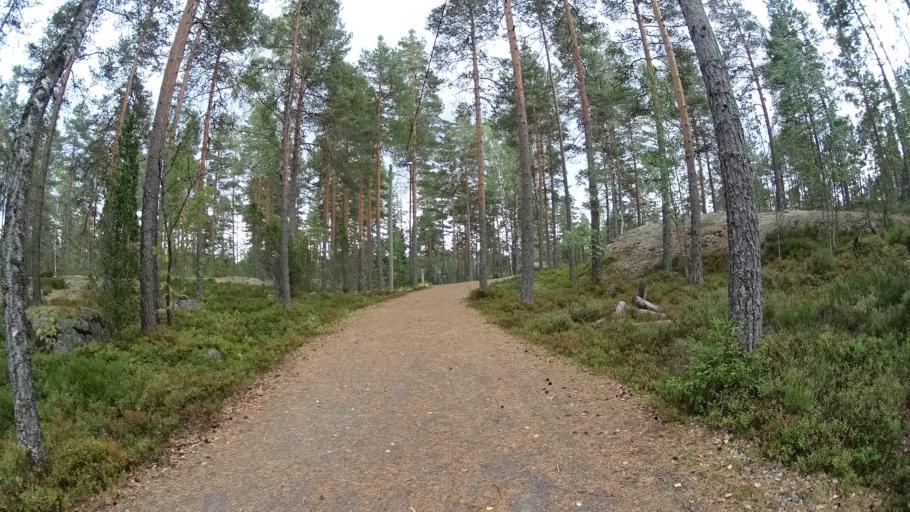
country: FI
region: Uusimaa
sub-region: Helsinki
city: Espoo
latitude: 60.2968
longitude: 24.5651
